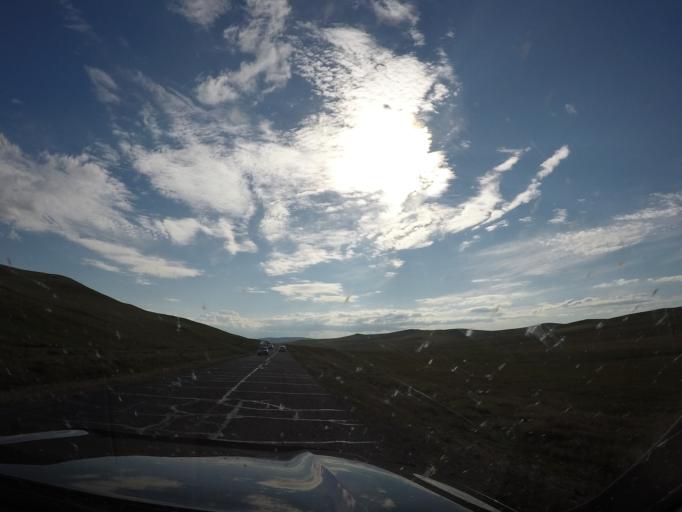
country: MN
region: Hentiy
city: Modot
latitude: 47.7919
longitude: 108.6818
